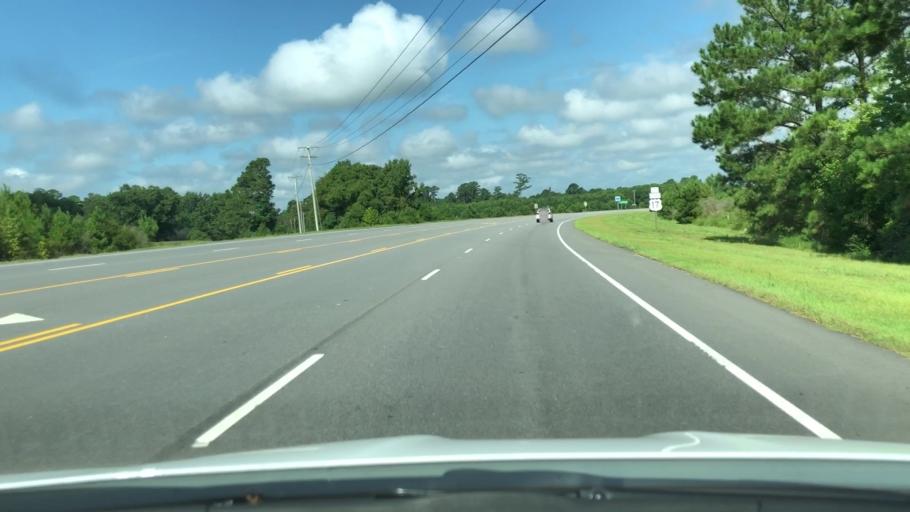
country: US
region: North Carolina
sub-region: Bertie County
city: Windsor
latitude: 36.0175
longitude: -76.8376
